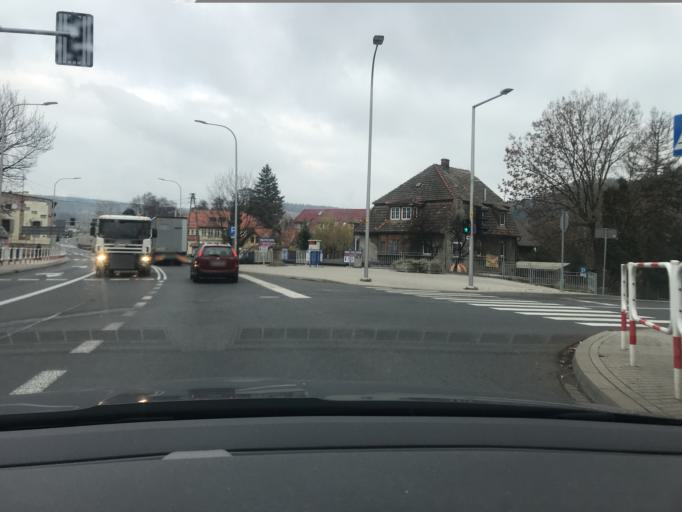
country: PL
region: Lower Silesian Voivodeship
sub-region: Powiat klodzki
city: Szczytna
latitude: 50.4126
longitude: 16.4466
